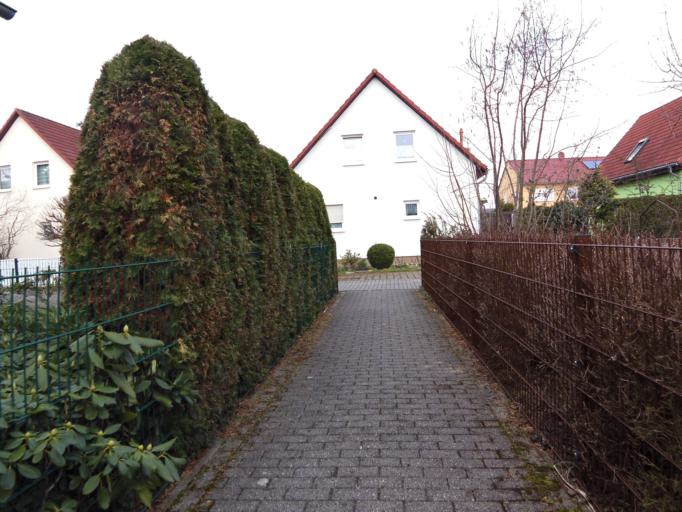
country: DE
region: Saxony
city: Markranstadt
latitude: 51.3084
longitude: 12.2925
